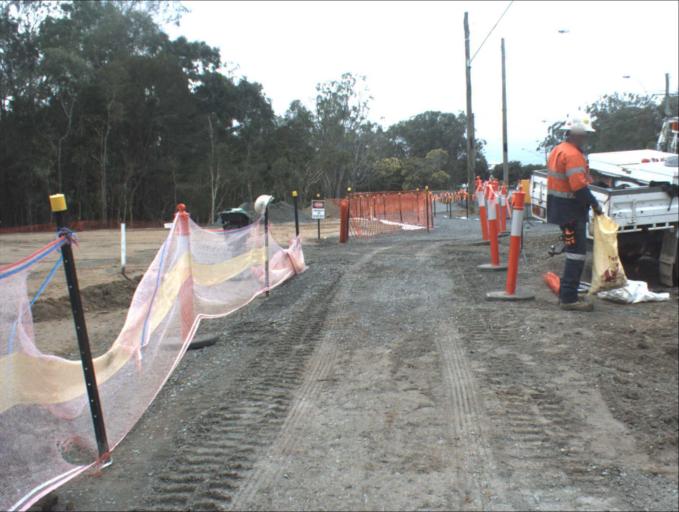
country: AU
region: Queensland
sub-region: Logan
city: Woodridge
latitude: -27.6732
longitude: 153.0724
